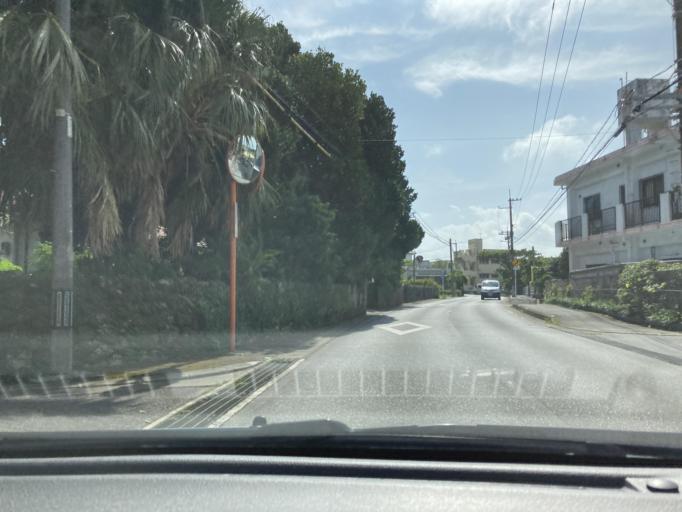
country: JP
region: Okinawa
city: Chatan
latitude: 26.2924
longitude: 127.7978
